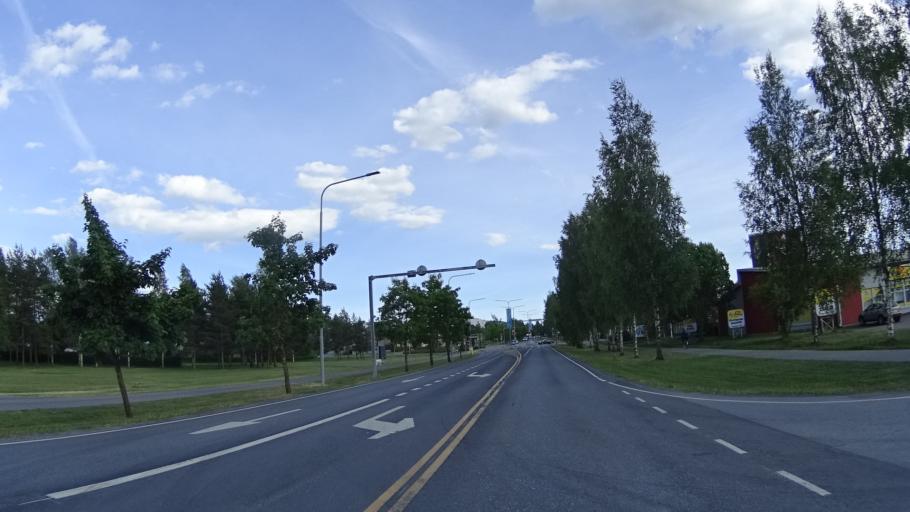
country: FI
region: Haeme
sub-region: Forssa
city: Forssa
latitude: 60.8232
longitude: 23.6284
